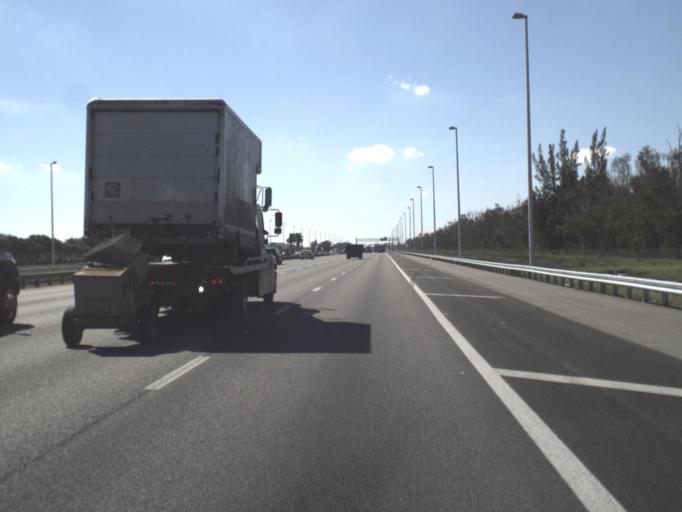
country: US
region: Florida
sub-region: Miami-Dade County
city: Doral
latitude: 25.8660
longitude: -80.3880
